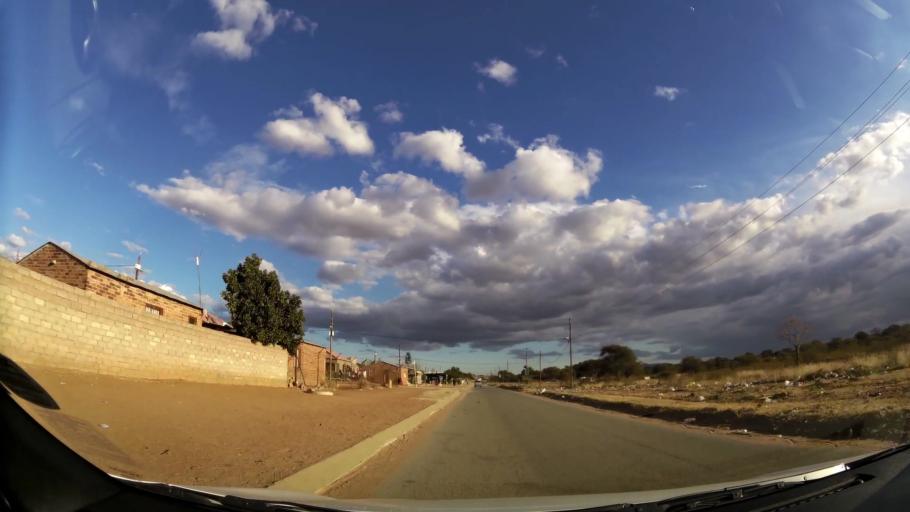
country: ZA
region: Limpopo
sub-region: Capricorn District Municipality
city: Polokwane
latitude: -23.9134
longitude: 29.4233
